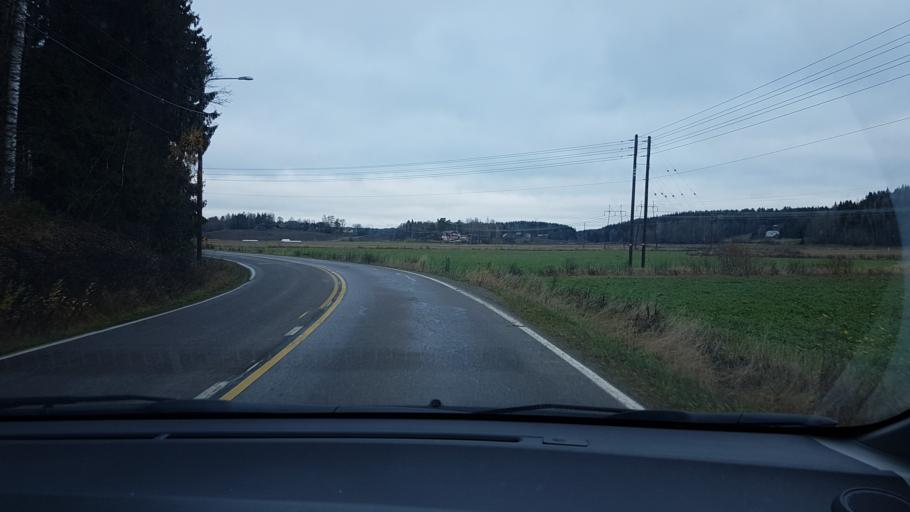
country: FI
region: Uusimaa
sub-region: Helsinki
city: Vantaa
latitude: 60.2742
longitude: 25.1387
